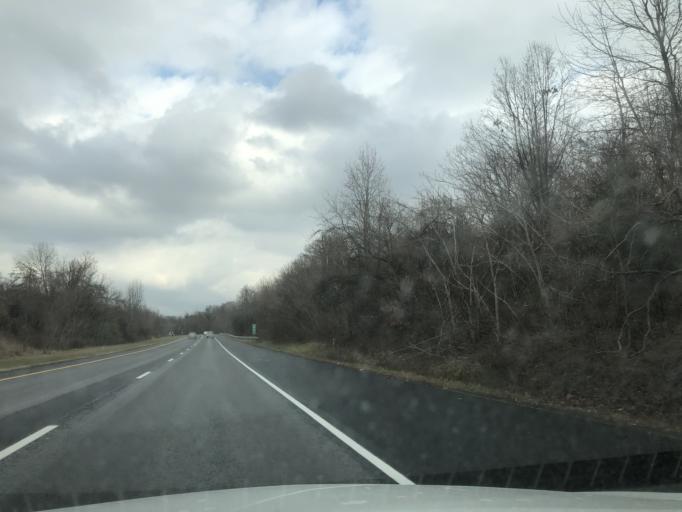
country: US
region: New Jersey
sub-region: Camden County
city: Glendora
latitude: 39.8357
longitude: -75.1013
